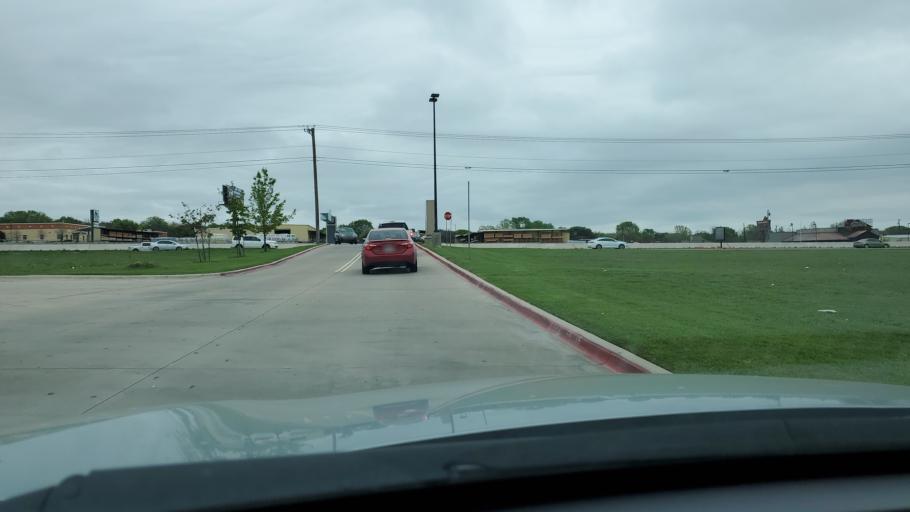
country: US
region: Texas
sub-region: Bell County
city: Harker Heights
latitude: 31.0723
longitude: -97.6798
